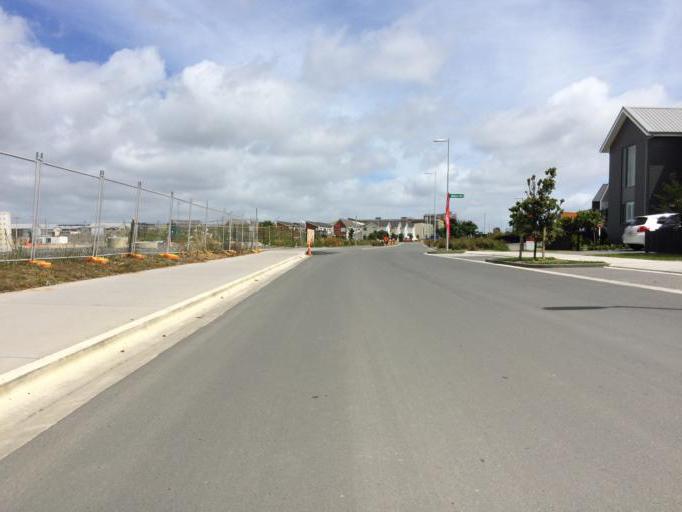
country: NZ
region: Auckland
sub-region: Auckland
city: Rosebank
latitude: -36.7947
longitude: 174.6642
